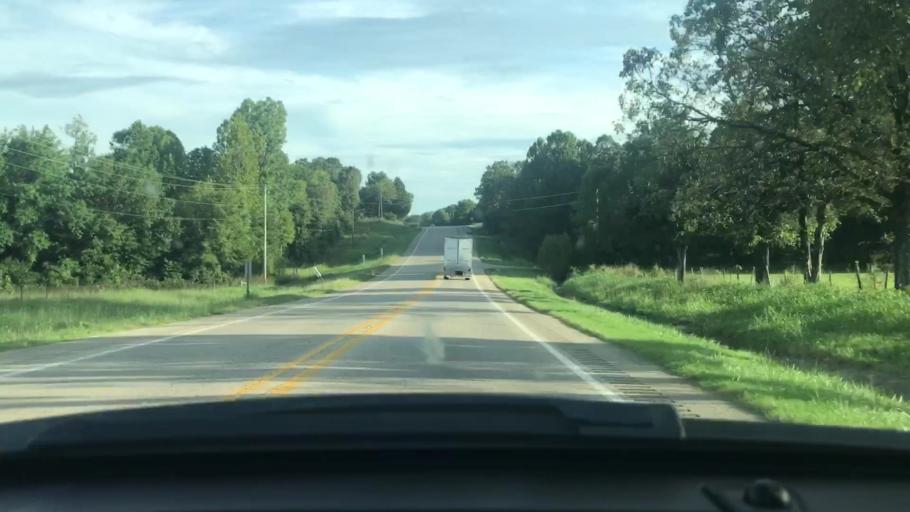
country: US
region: Arkansas
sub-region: Lawrence County
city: Hoxie
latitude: 36.1580
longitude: -91.1619
